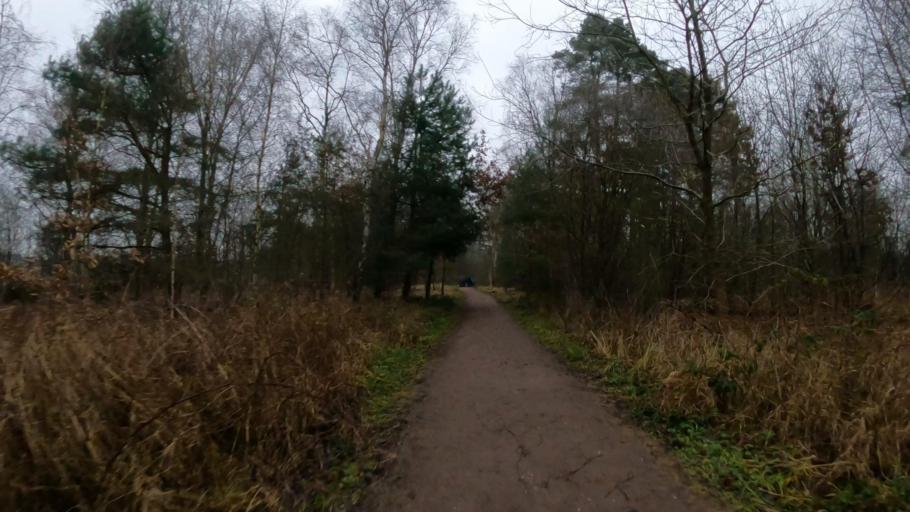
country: DE
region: Schleswig-Holstein
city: Appen
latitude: 53.6013
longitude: 9.7553
